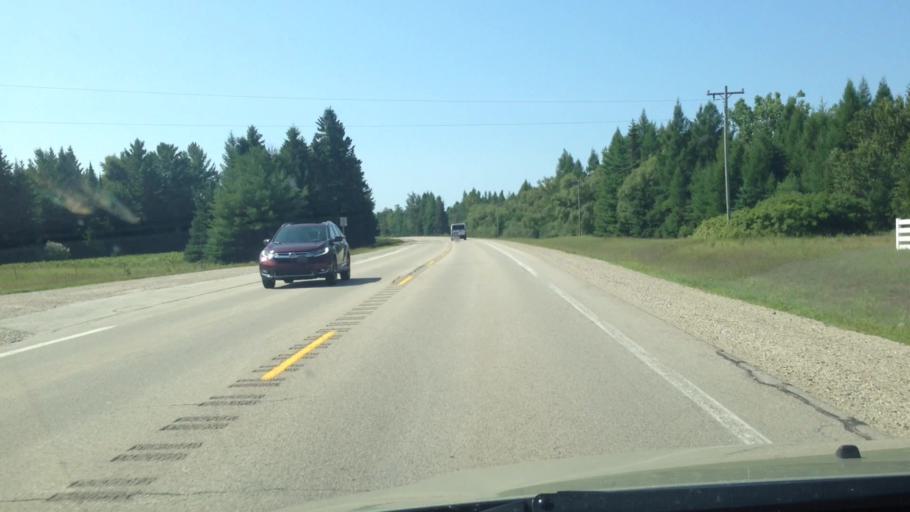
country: US
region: Michigan
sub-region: Delta County
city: Escanaba
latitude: 45.5231
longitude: -87.2882
